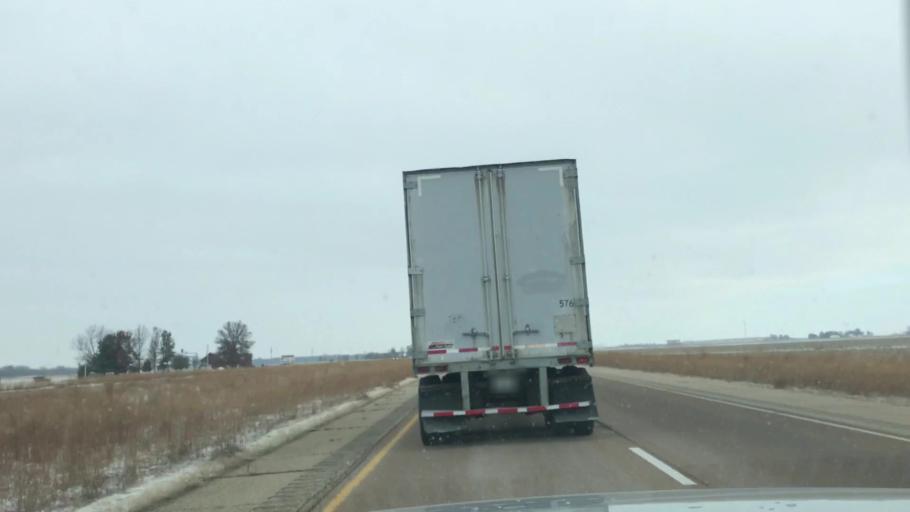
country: US
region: Illinois
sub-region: Montgomery County
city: Raymond
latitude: 39.3997
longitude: -89.6430
